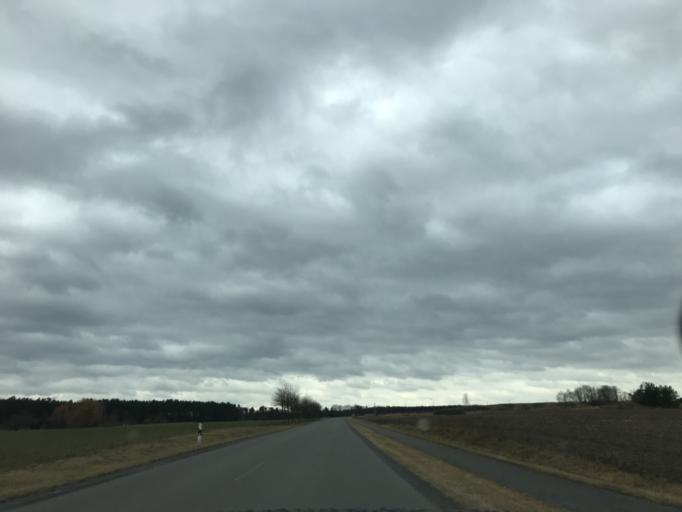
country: DE
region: Brandenburg
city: Crinitz
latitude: 51.7580
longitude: 13.8129
